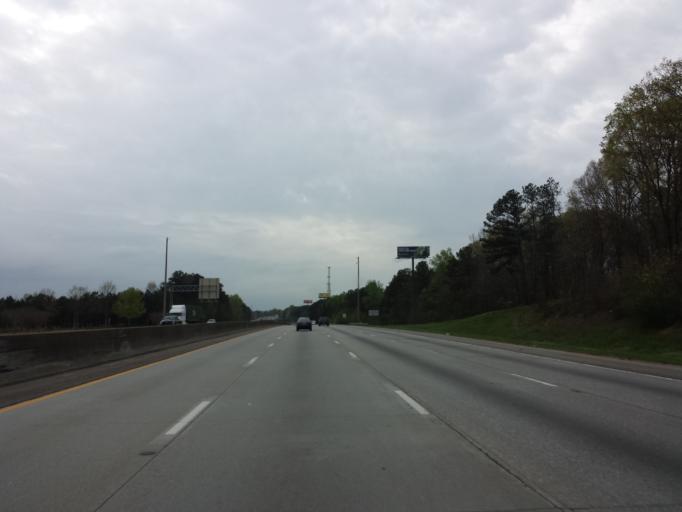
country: US
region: Georgia
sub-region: Henry County
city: Stockbridge
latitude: 33.5514
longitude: -84.2898
